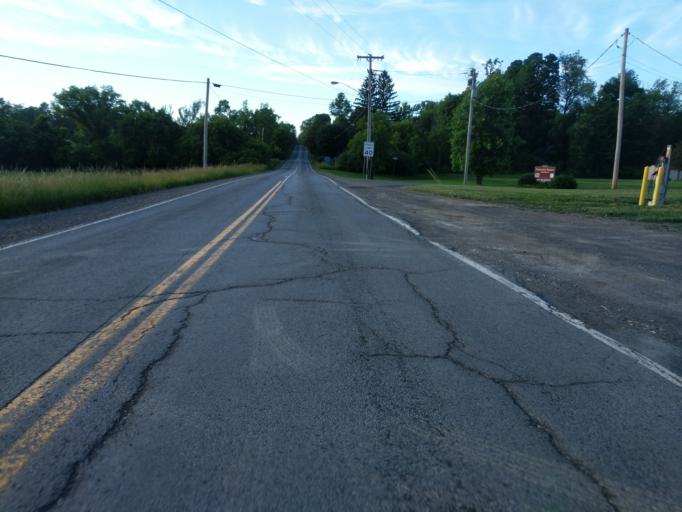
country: US
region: New York
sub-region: Tompkins County
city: Dryden
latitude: 42.3942
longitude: -76.3506
